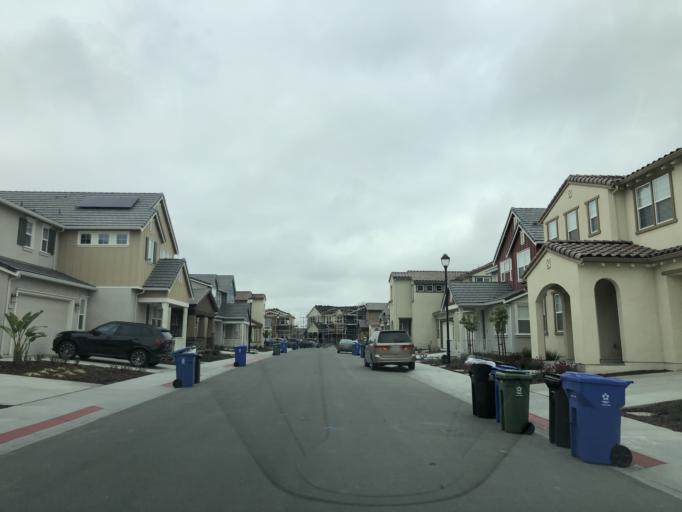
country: US
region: California
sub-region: Alameda County
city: Fremont
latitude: 37.5139
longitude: -121.9962
